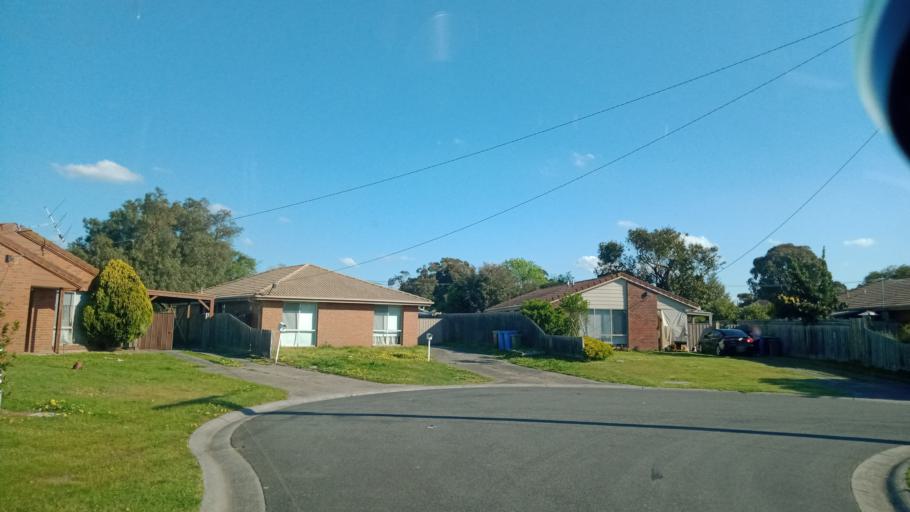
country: AU
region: Victoria
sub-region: Casey
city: Cranbourne North
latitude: -38.0901
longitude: 145.2750
